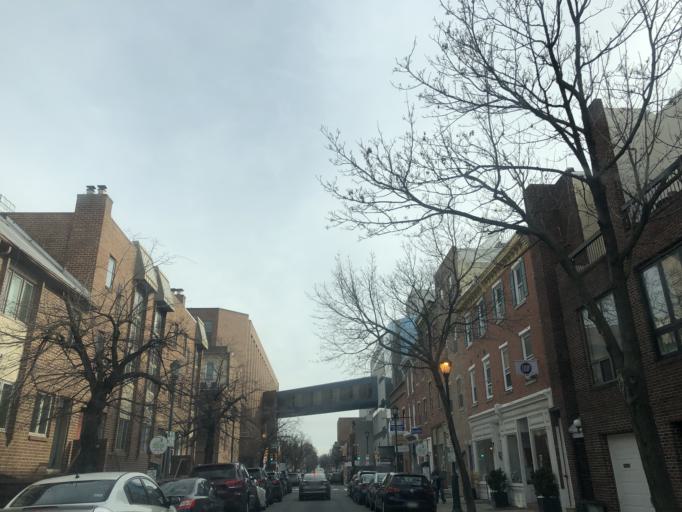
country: US
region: Pennsylvania
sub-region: Philadelphia County
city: Philadelphia
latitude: 39.9447
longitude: -75.1744
